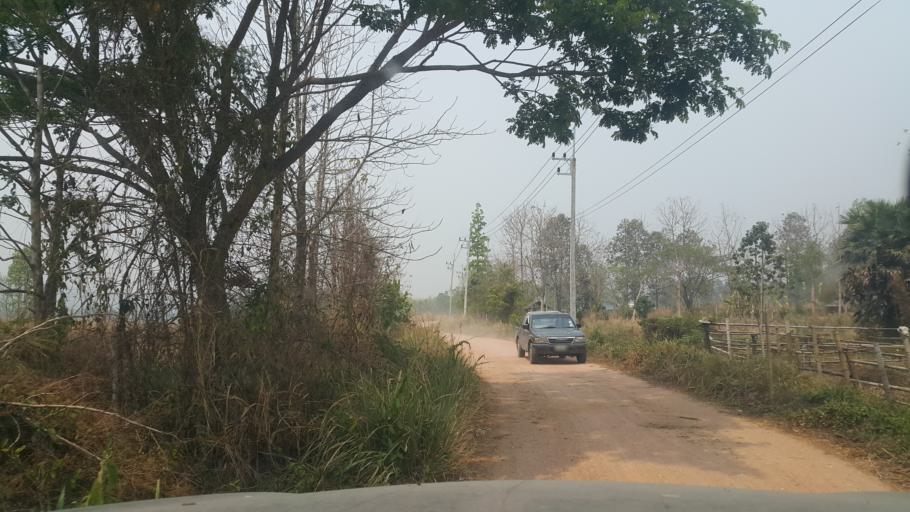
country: TH
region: Lampang
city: Hang Chat
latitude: 18.2949
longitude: 99.2562
